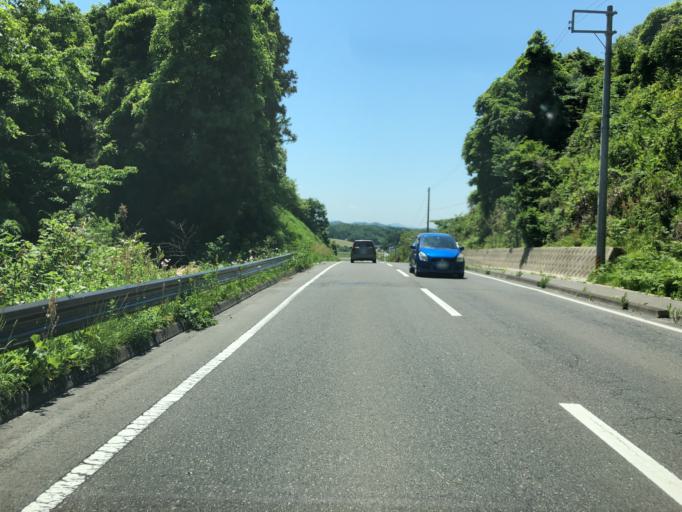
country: JP
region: Fukushima
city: Motomiya
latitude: 37.5157
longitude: 140.4585
